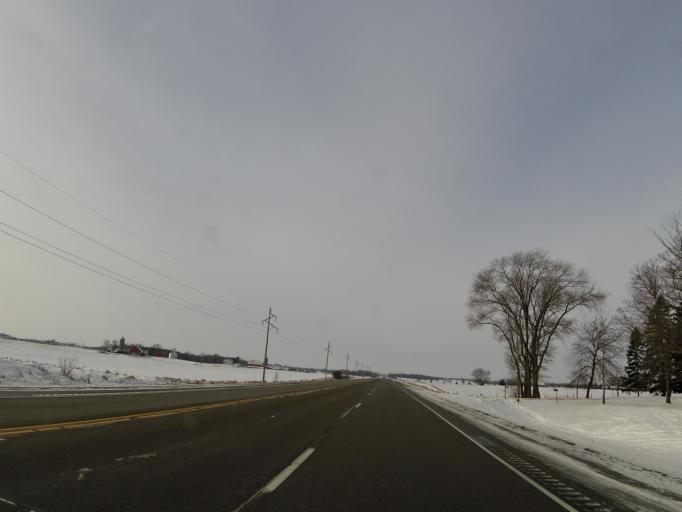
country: US
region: Minnesota
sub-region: Carver County
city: Watertown
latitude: 44.9056
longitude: -93.8294
